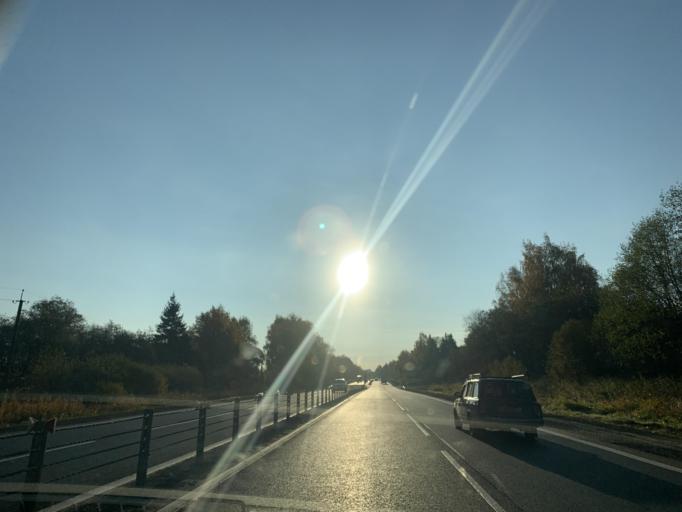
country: RU
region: Jaroslavl
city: Konstantinovskiy
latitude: 57.7836
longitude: 39.6234
